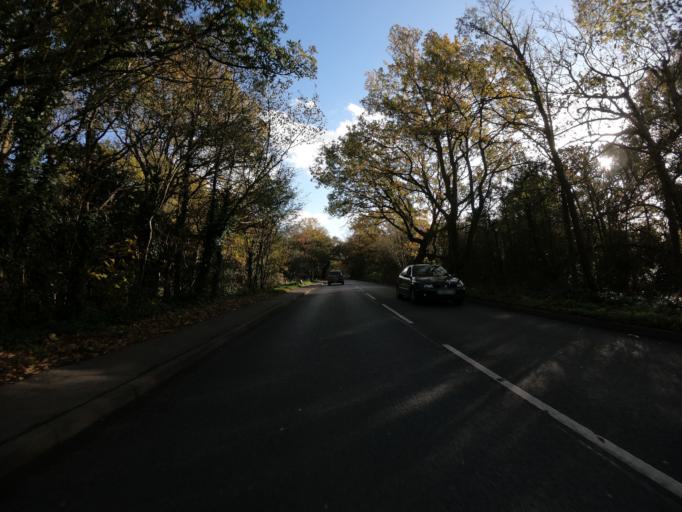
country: GB
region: England
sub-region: Greater London
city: Chislehurst
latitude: 51.4075
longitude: 0.0822
